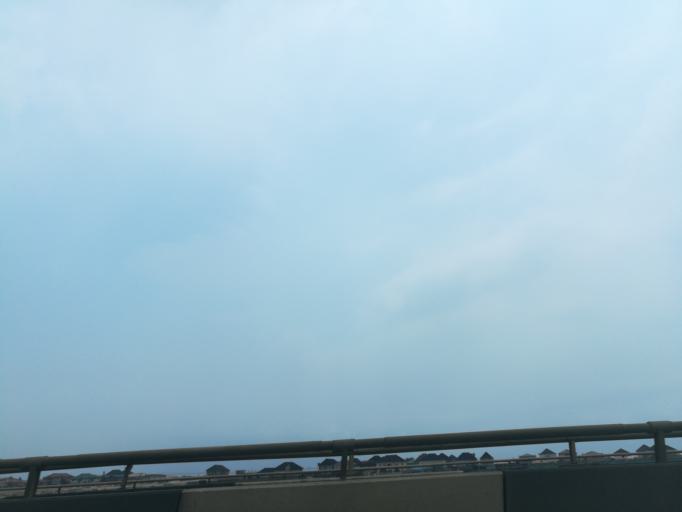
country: NG
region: Lagos
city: Somolu
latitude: 6.5358
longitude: 3.4004
